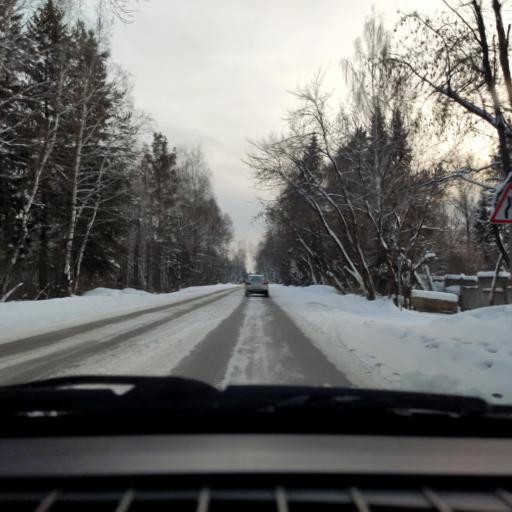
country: RU
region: Perm
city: Overyata
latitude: 58.0524
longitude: 55.8841
